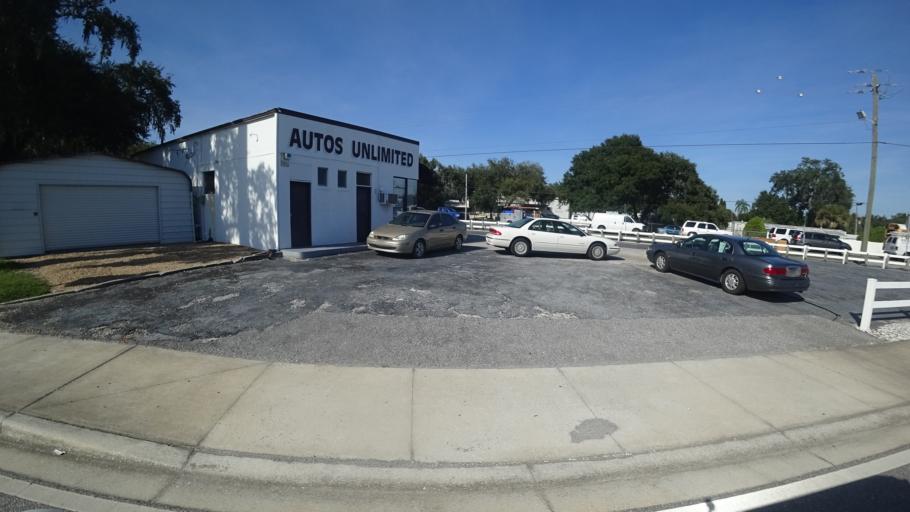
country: US
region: Florida
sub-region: Manatee County
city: West Samoset
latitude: 27.4624
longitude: -82.5586
